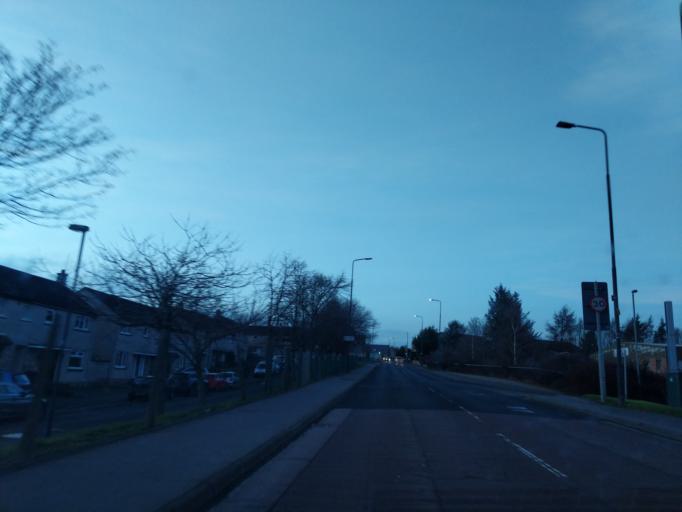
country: GB
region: Scotland
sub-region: Midlothian
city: Bonnyrigg
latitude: 55.8722
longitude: -3.0992
